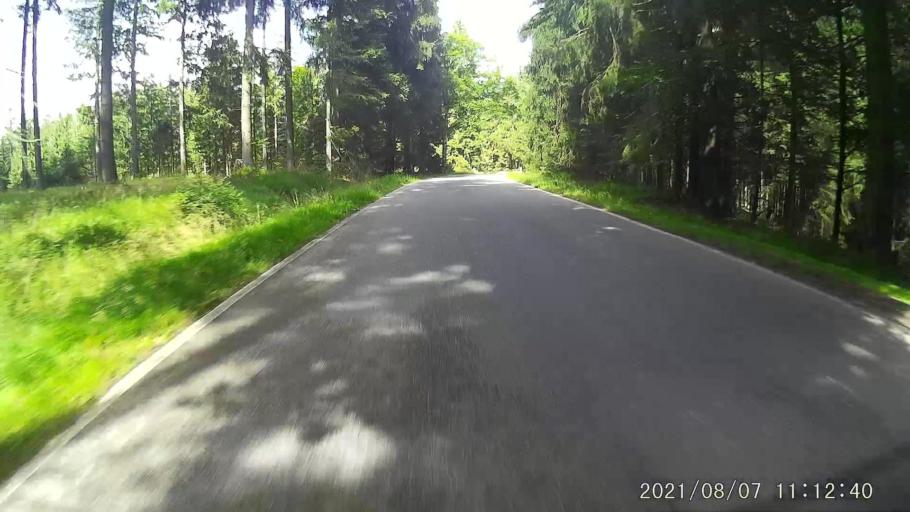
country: CZ
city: Rokytnice v Orlickych Horach
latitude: 50.2751
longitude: 16.5157
